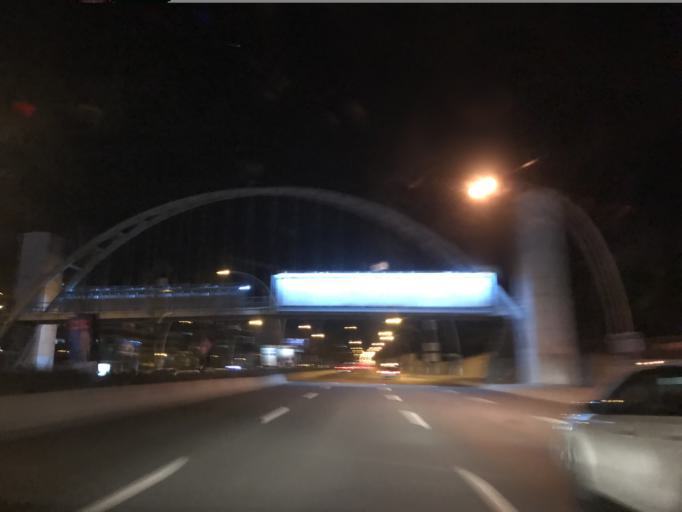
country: TR
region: Ankara
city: Ankara
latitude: 39.8807
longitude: 32.8116
